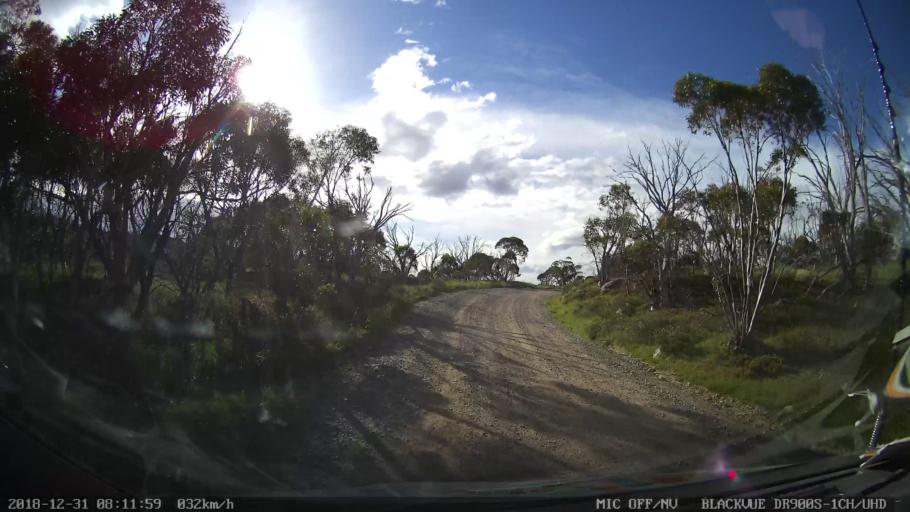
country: AU
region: New South Wales
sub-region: Snowy River
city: Jindabyne
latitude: -36.3857
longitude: 148.4298
